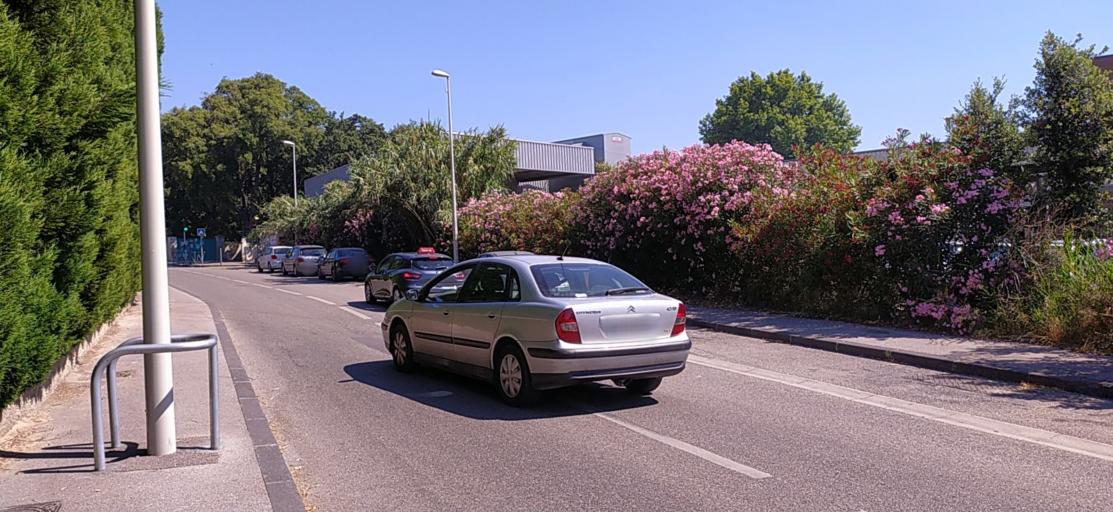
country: FR
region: Provence-Alpes-Cote d'Azur
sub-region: Departement des Bouches-du-Rhone
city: Marseille 16
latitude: 43.3574
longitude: 5.3338
